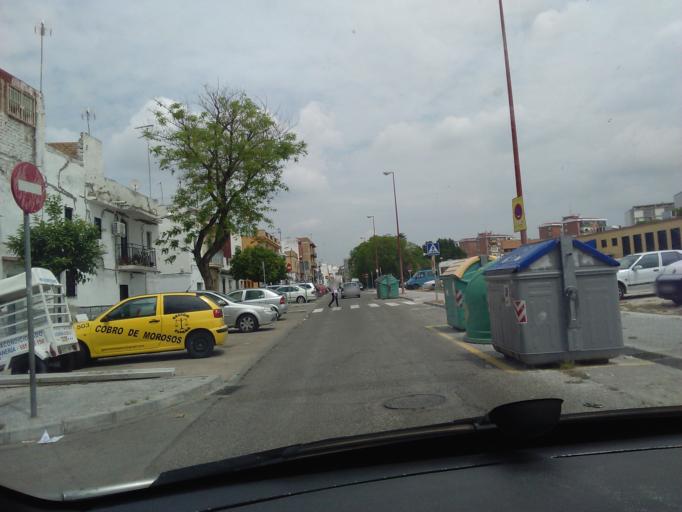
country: ES
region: Andalusia
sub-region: Provincia de Sevilla
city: Sevilla
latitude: 37.3712
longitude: -5.9458
